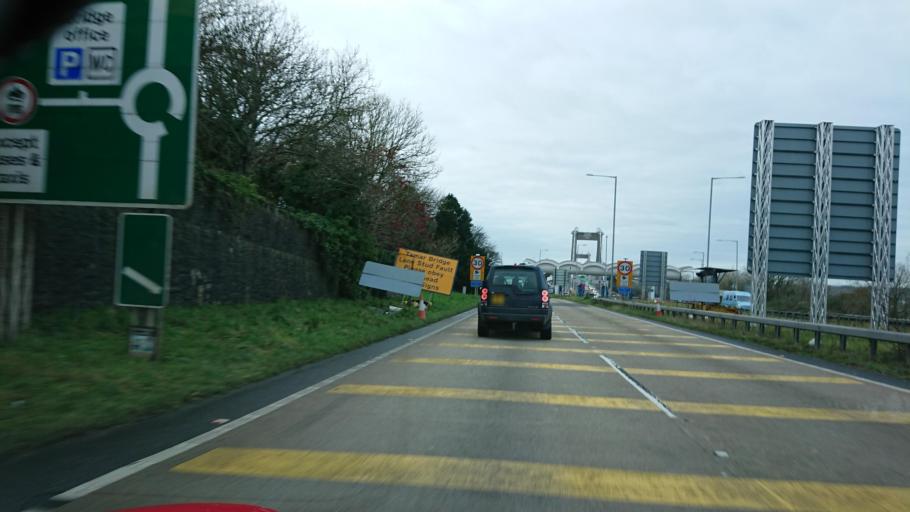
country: GB
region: England
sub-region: Cornwall
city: Saltash
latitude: 50.4075
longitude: -4.1957
